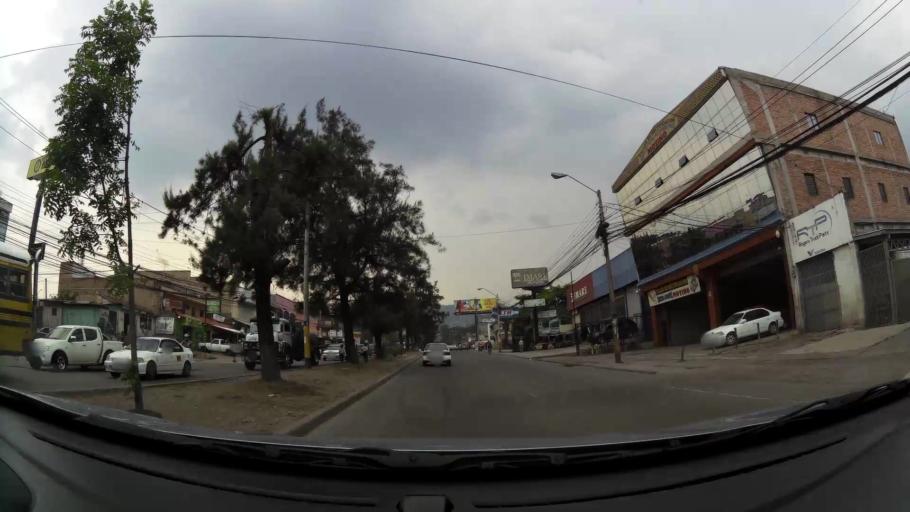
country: HN
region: Francisco Morazan
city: Tegucigalpa
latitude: 14.0995
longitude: -87.2287
